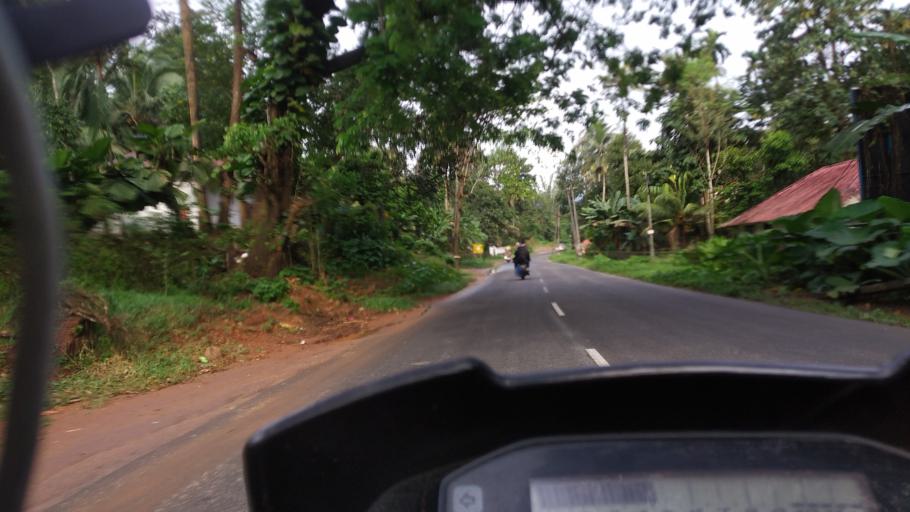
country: IN
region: Kerala
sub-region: Ernakulam
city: Kotamangalam
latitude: 10.0502
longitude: 76.7244
